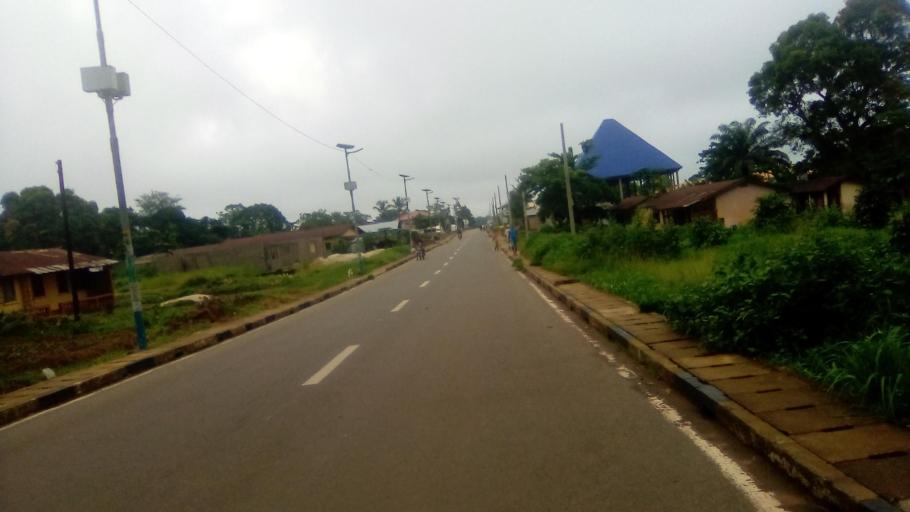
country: SL
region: Southern Province
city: Moyamba
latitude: 8.1607
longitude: -12.4361
